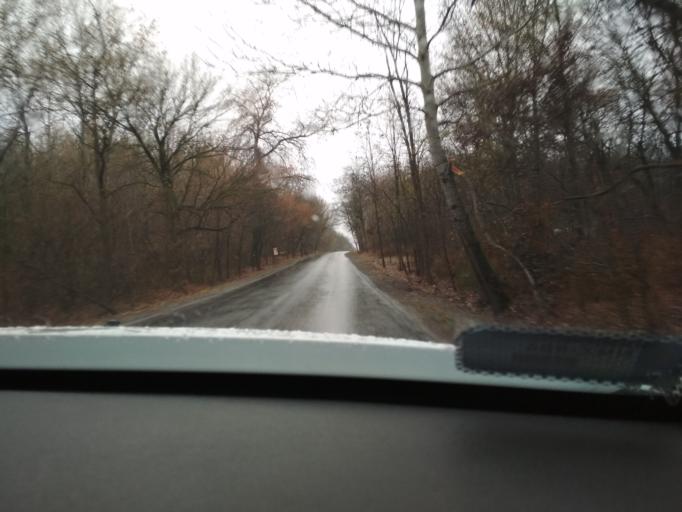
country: HU
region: Csongrad
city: Opusztaszer
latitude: 46.4398
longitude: 20.1209
